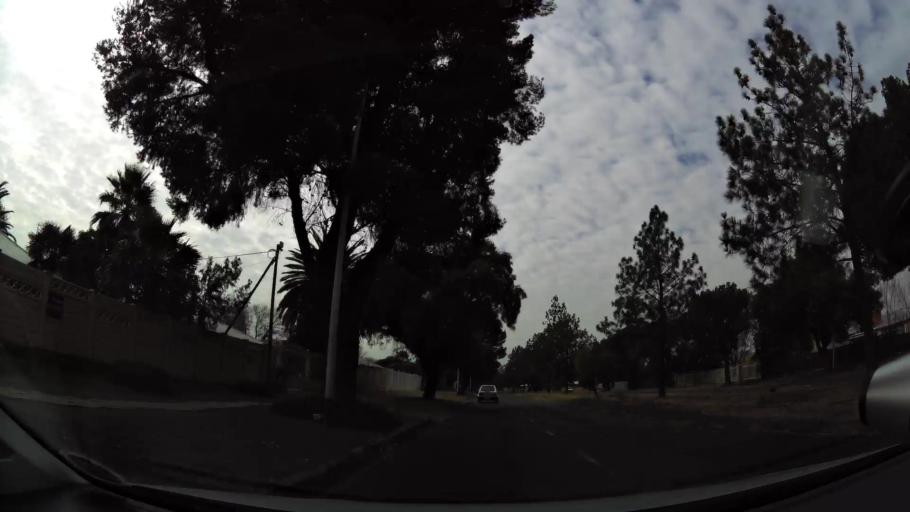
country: ZA
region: Orange Free State
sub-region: Mangaung Metropolitan Municipality
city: Bloemfontein
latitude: -29.1306
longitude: 26.1967
